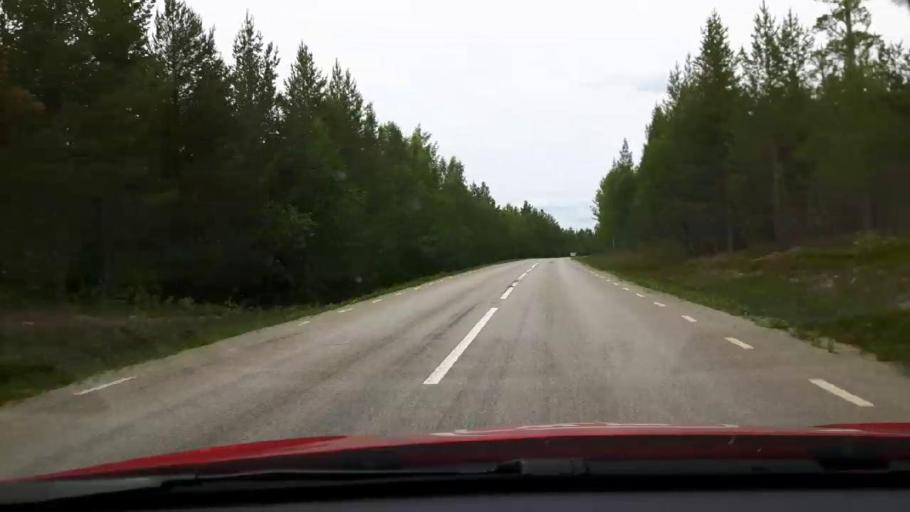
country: SE
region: Jaemtland
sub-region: Harjedalens Kommun
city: Sveg
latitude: 62.2432
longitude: 13.8459
